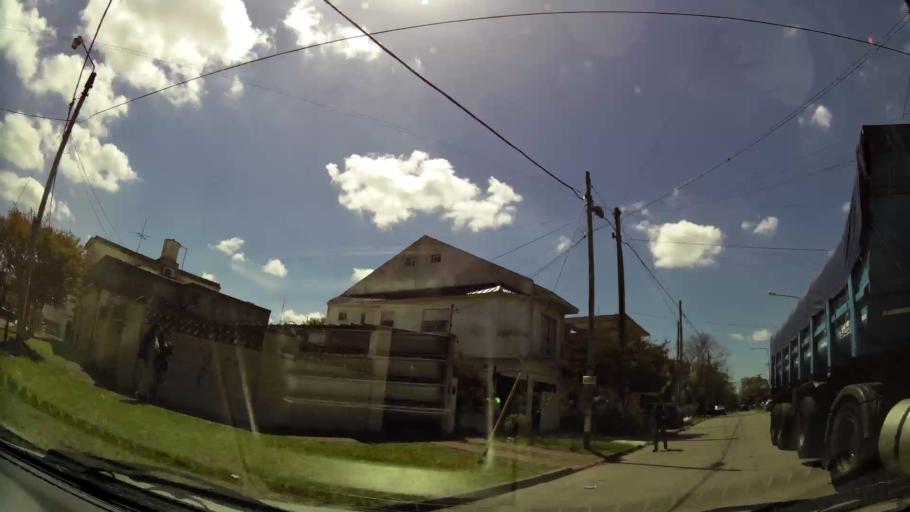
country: AR
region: Buenos Aires
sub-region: Partido de Quilmes
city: Quilmes
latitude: -34.8160
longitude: -58.2788
